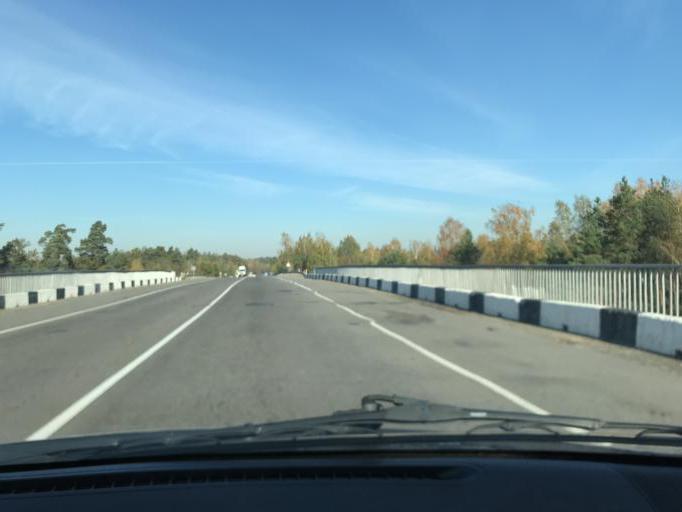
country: BY
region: Brest
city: Mikashevichy
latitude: 52.2432
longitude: 27.4448
